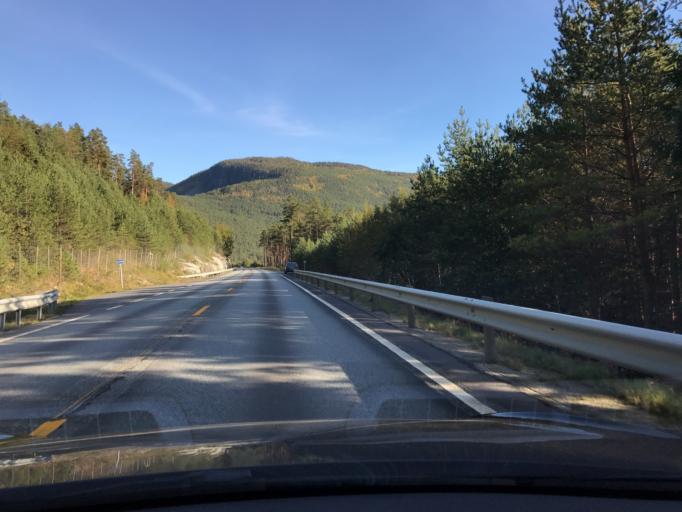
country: NO
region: Sogn og Fjordane
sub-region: Sogndal
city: Sogndalsfjora
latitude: 61.1818
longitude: 7.2780
